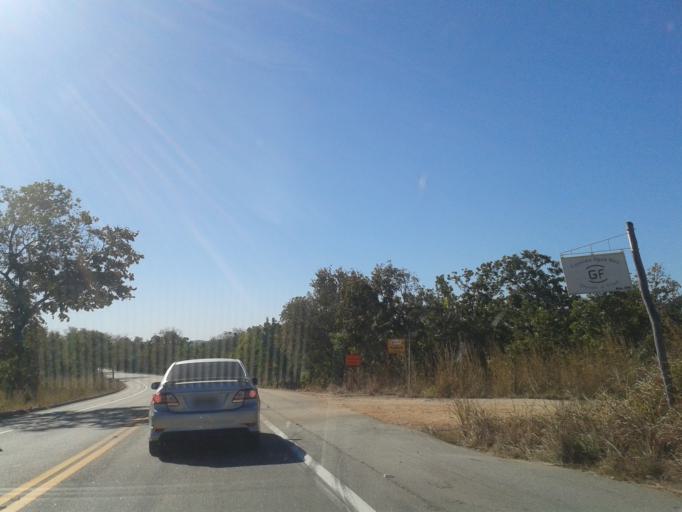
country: BR
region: Goias
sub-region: Itapuranga
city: Itapuranga
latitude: -15.5040
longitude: -50.3039
